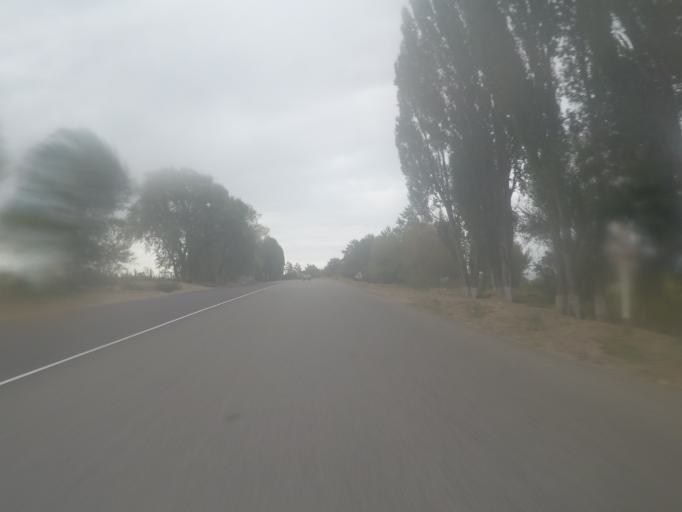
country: KG
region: Ysyk-Koel
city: Cholpon-Ata
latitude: 42.6688
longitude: 77.2839
